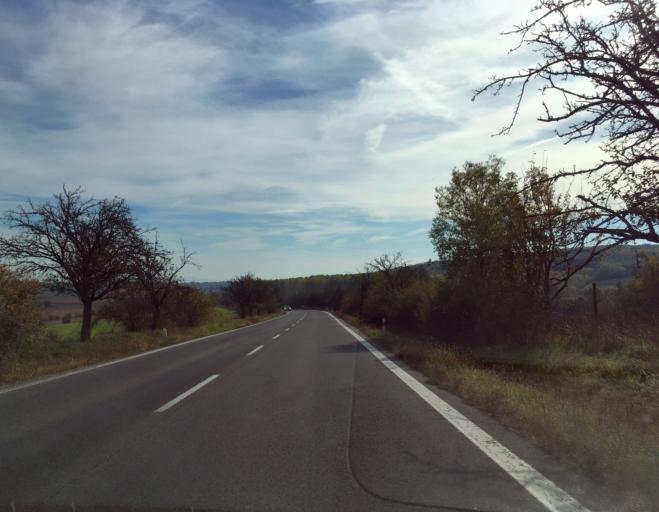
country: SK
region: Nitriansky
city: Svodin
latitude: 48.0344
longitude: 18.4424
